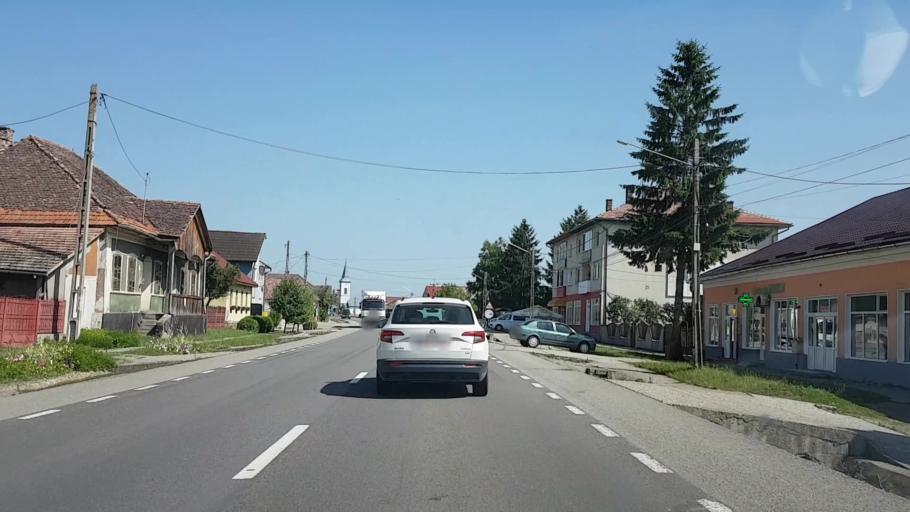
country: RO
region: Bistrita-Nasaud
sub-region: Comuna Sieu-Magherus
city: Sieu-Magherus
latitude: 47.0913
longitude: 24.3727
